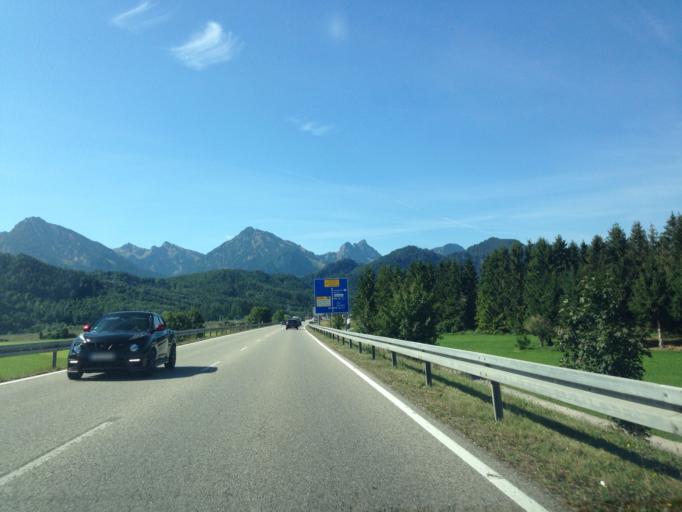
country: DE
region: Bavaria
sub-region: Swabia
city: Fuessen
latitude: 47.5762
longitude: 10.6690
